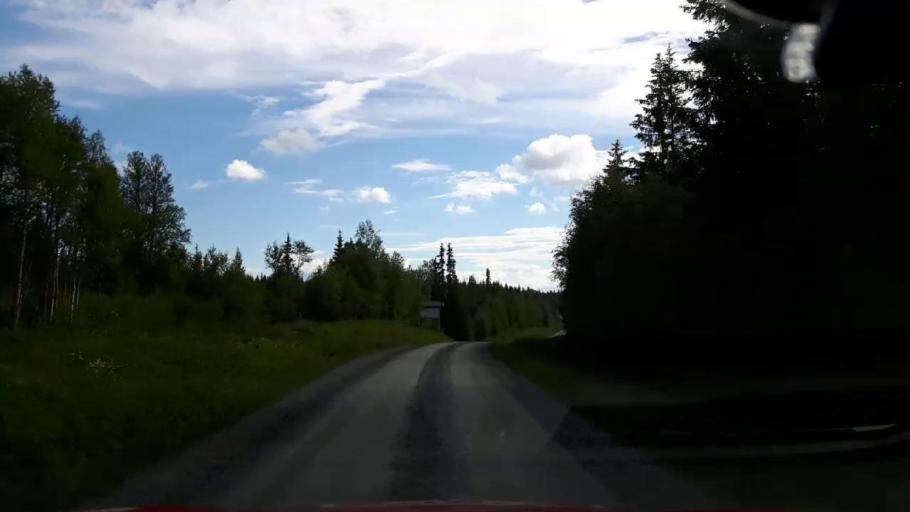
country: SE
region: Jaemtland
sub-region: Krokoms Kommun
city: Valla
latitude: 63.8705
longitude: 14.1205
